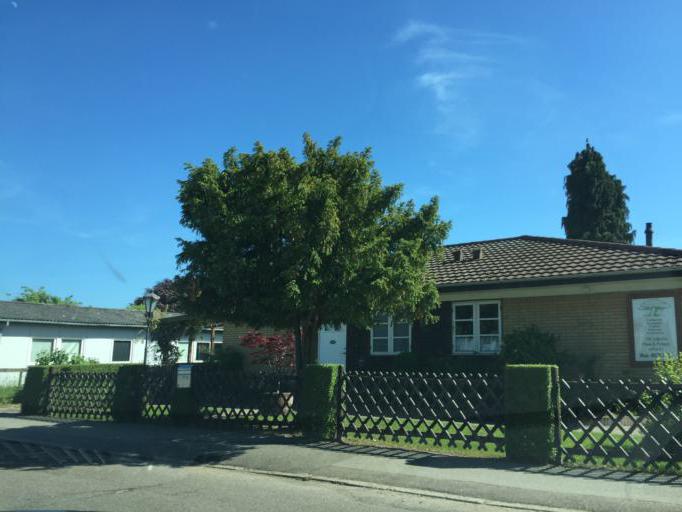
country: DK
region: Zealand
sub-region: Stevns Kommune
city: Harlev
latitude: 55.3502
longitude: 12.2308
